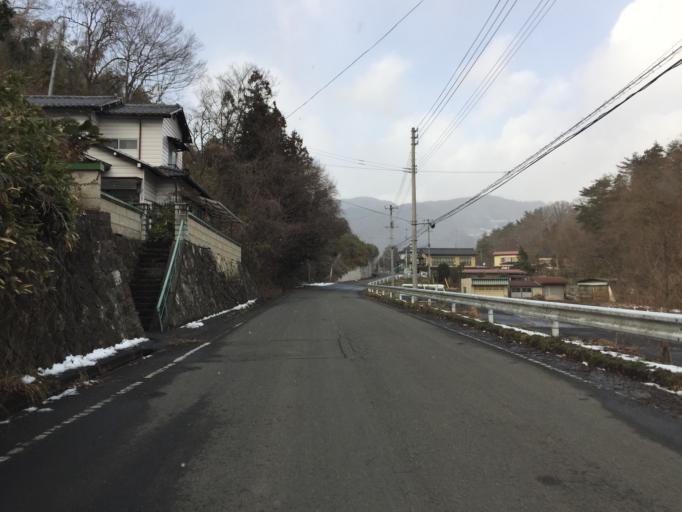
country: JP
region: Fukushima
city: Fukushima-shi
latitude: 37.8344
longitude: 140.4565
